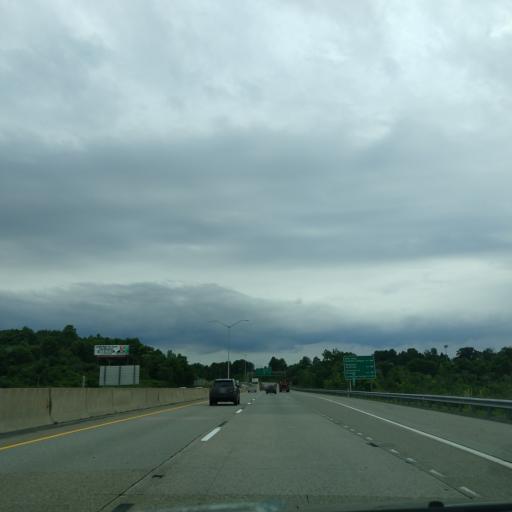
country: US
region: Pennsylvania
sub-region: Lackawanna County
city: Throop
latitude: 41.4404
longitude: -75.6289
